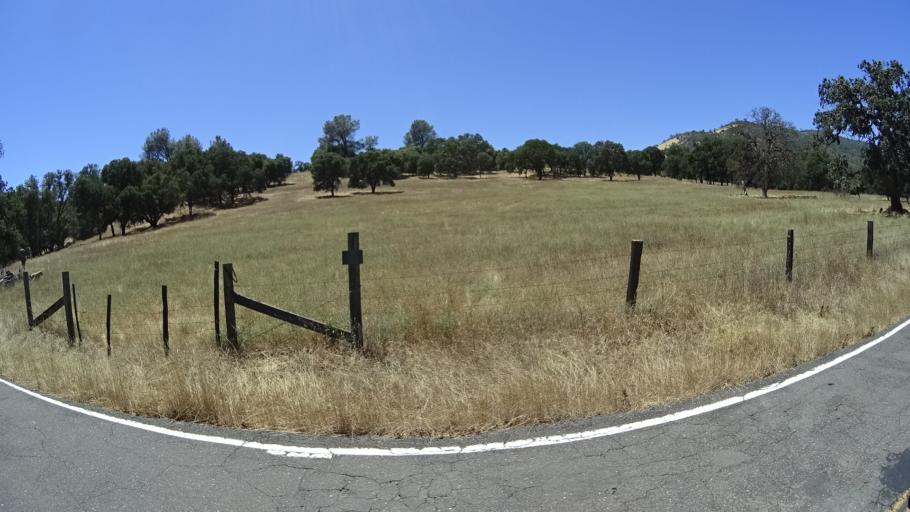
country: US
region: California
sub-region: Calaveras County
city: San Andreas
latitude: 38.1229
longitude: -120.6585
